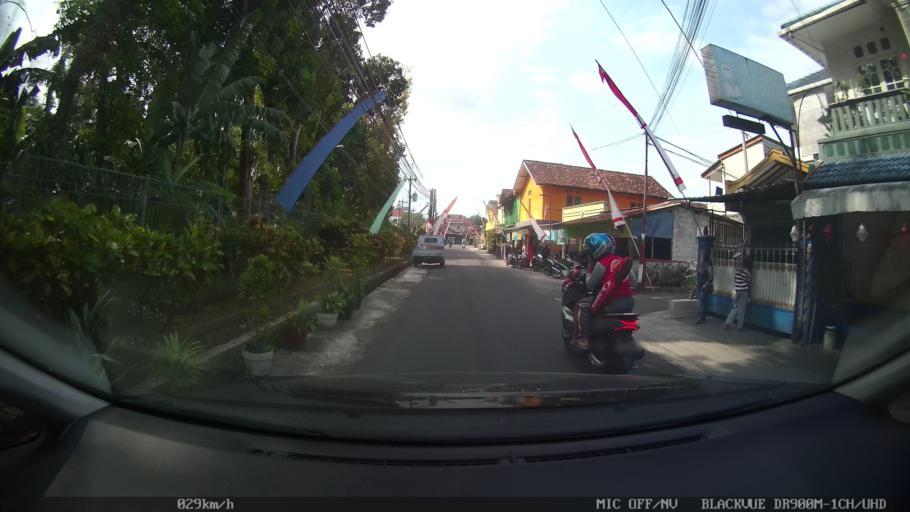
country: ID
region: Daerah Istimewa Yogyakarta
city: Depok
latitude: -7.7545
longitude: 110.4230
